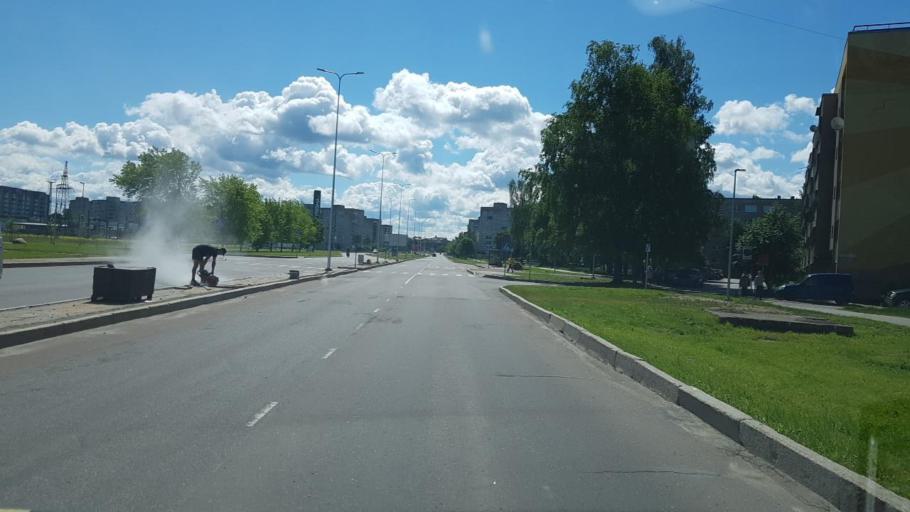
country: EE
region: Ida-Virumaa
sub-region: Narva linn
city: Narva
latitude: 59.3894
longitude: 28.1729
